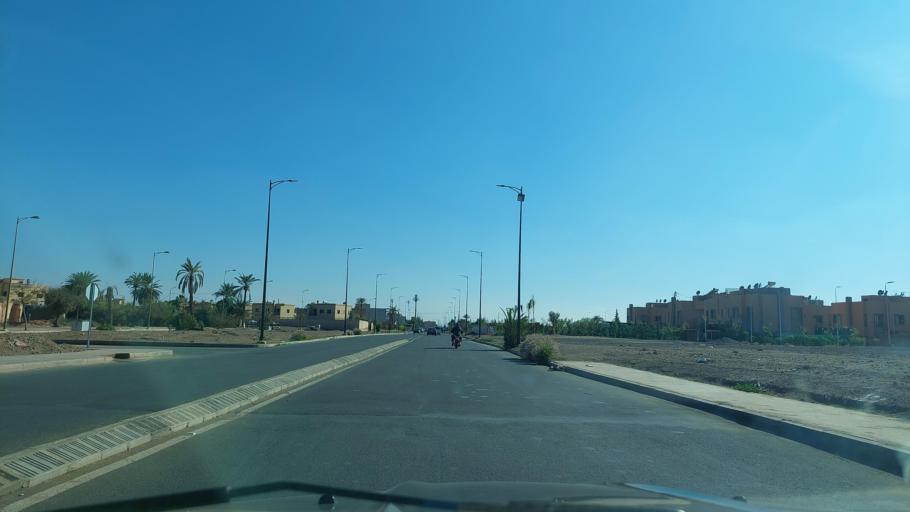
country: MA
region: Marrakech-Tensift-Al Haouz
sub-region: Marrakech
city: Marrakesh
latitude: 31.6583
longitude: -8.0660
